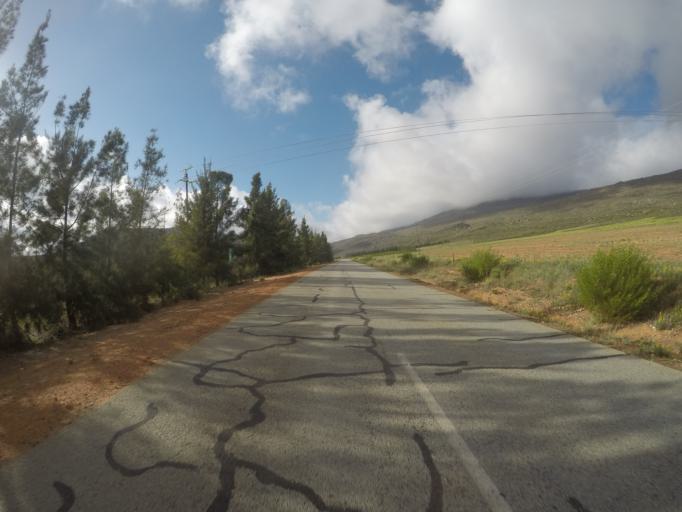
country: ZA
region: Western Cape
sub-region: West Coast District Municipality
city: Clanwilliam
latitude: -32.3509
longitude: 18.8479
